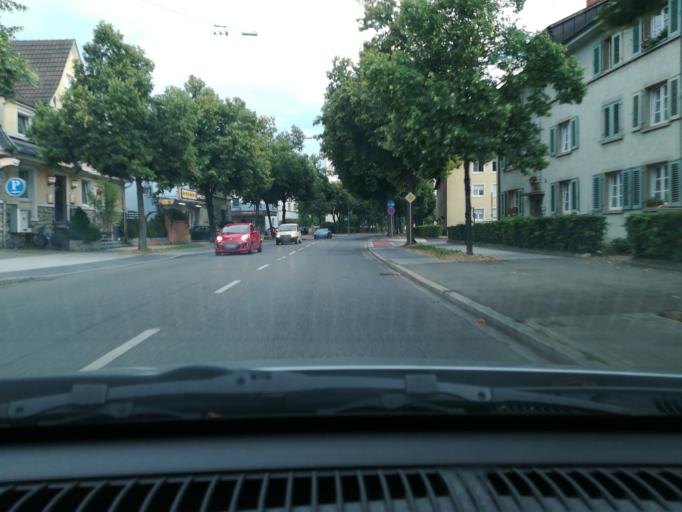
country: DE
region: Baden-Wuerttemberg
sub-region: Freiburg Region
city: Singen
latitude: 47.7505
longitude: 8.8426
